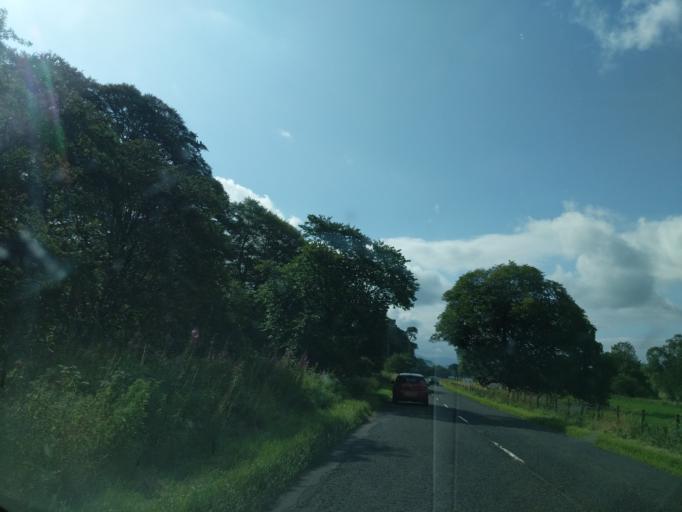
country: GB
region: Scotland
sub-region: The Scottish Borders
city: Peebles
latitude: 55.7340
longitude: -3.2061
